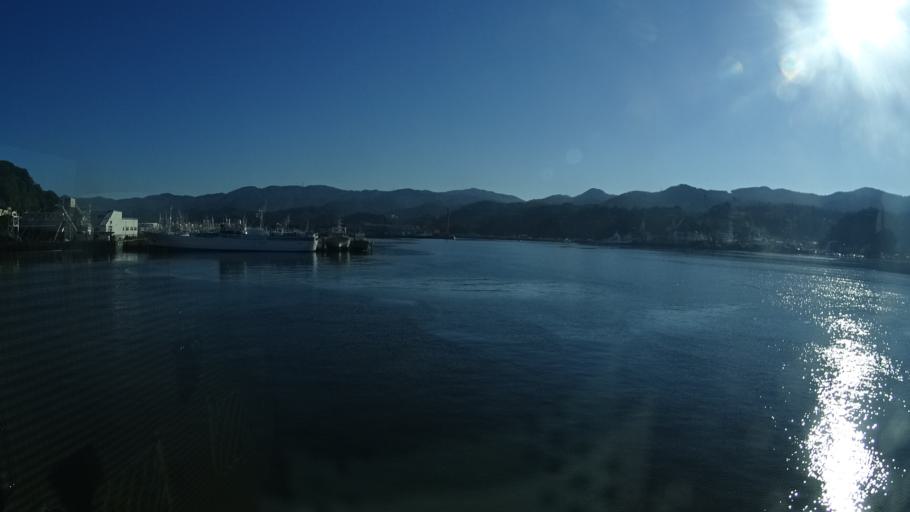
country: JP
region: Iwate
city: Ofunato
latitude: 38.9051
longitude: 141.5804
